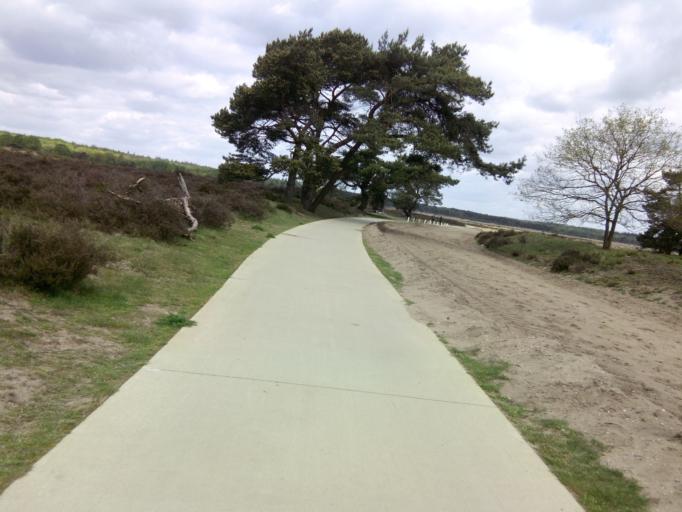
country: NL
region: Gelderland
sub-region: Gemeente Ede
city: Ede
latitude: 52.0502
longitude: 5.7075
